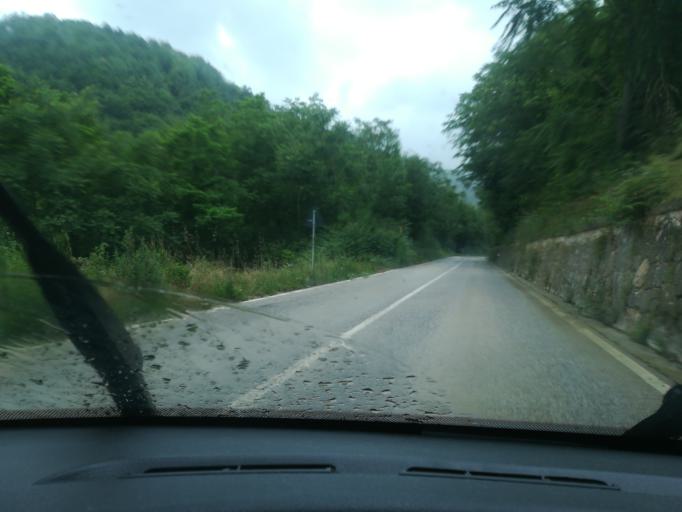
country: IT
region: The Marches
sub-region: Province of Fermo
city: Amandola
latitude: 42.9833
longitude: 13.3469
